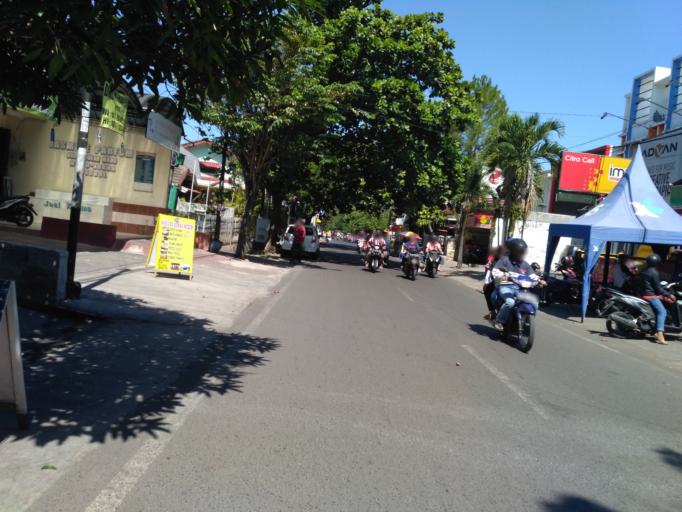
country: ID
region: East Java
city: Malang
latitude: -7.9761
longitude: 112.6651
